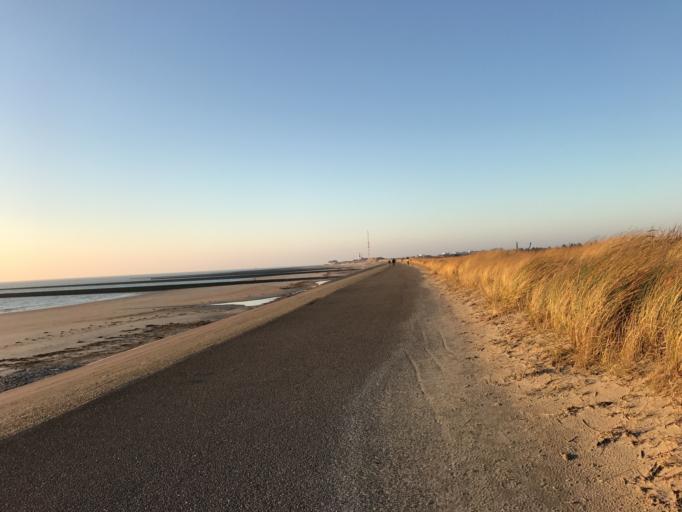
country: DE
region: Lower Saxony
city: Borkum
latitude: 53.5698
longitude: 6.6899
